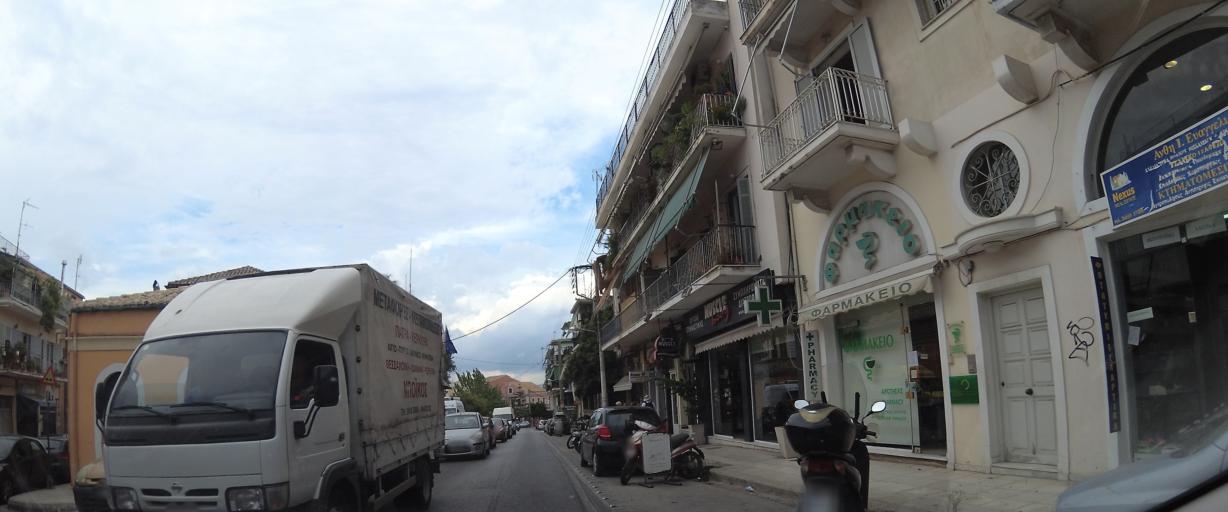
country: GR
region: Ionian Islands
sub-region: Nomos Kerkyras
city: Kerkyra
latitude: 39.6226
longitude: 19.9102
